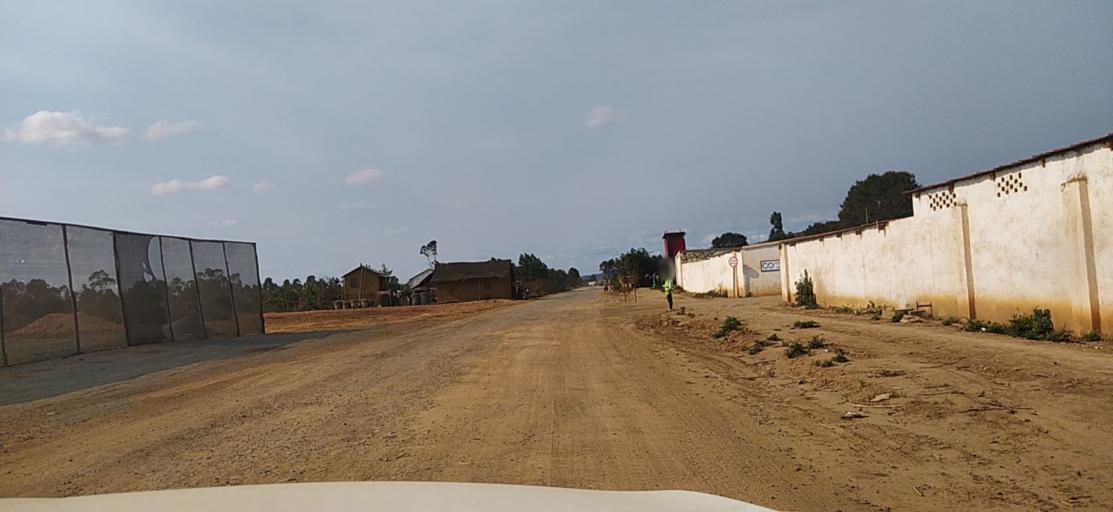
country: MG
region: Alaotra Mangoro
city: Moramanga
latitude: -18.6739
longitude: 48.2733
